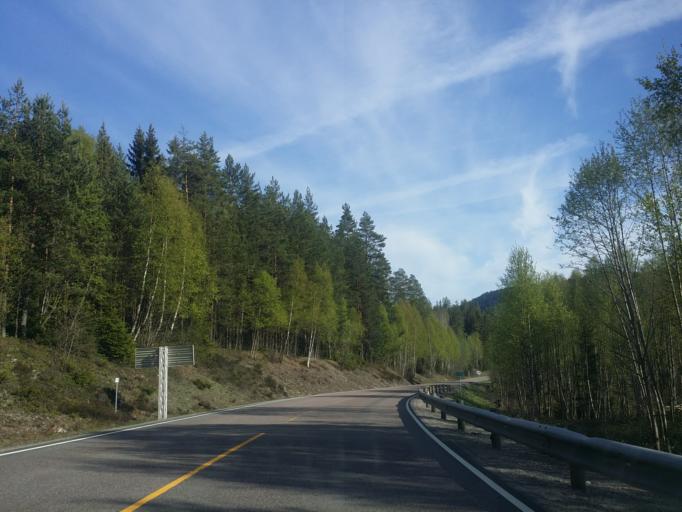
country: NO
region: Telemark
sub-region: Hjartdal
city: Sauland
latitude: 59.6104
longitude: 9.0195
